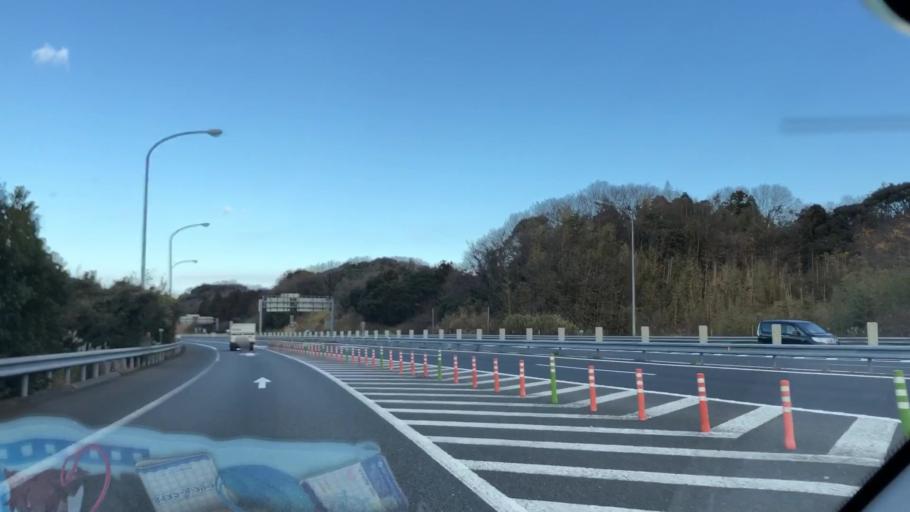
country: JP
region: Chiba
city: Kisarazu
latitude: 35.3804
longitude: 139.9778
